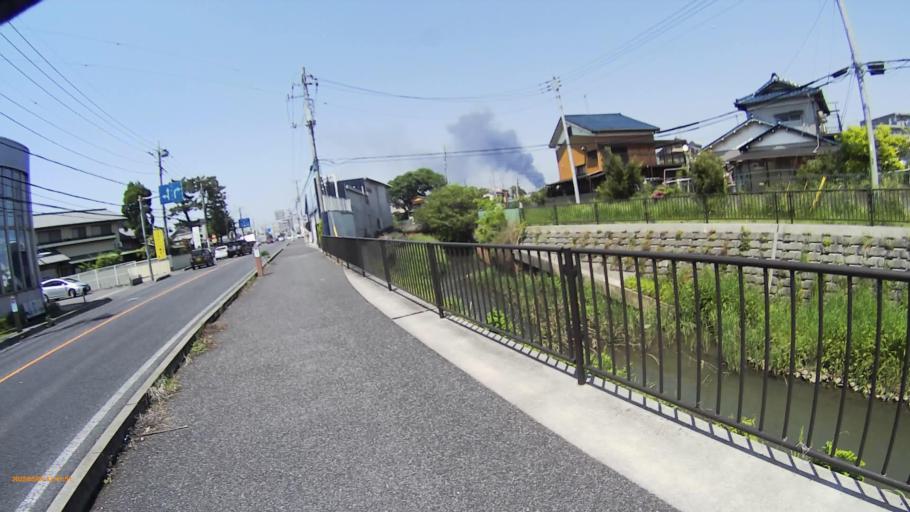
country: JP
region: Saitama
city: Kasukabe
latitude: 35.9442
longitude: 139.7762
